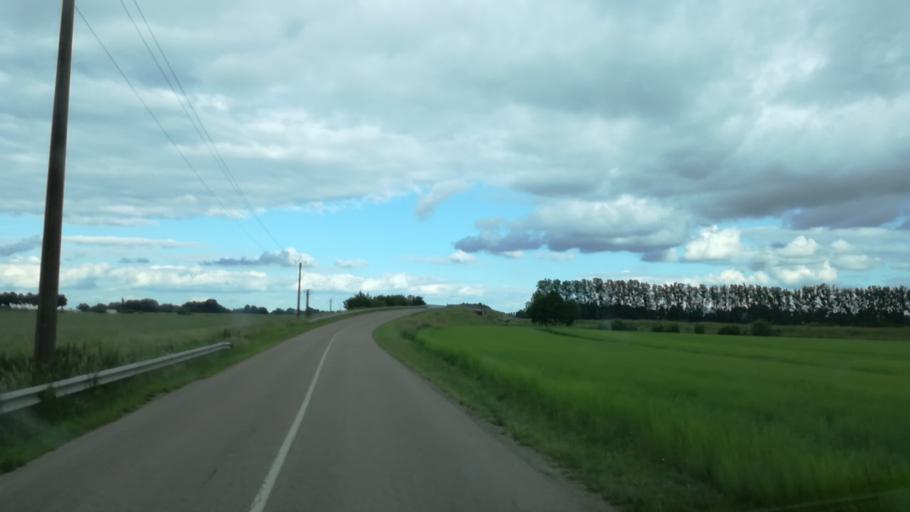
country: FR
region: Haute-Normandie
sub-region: Departement de l'Eure
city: Bourg-Achard
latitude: 49.3027
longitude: 0.7962
